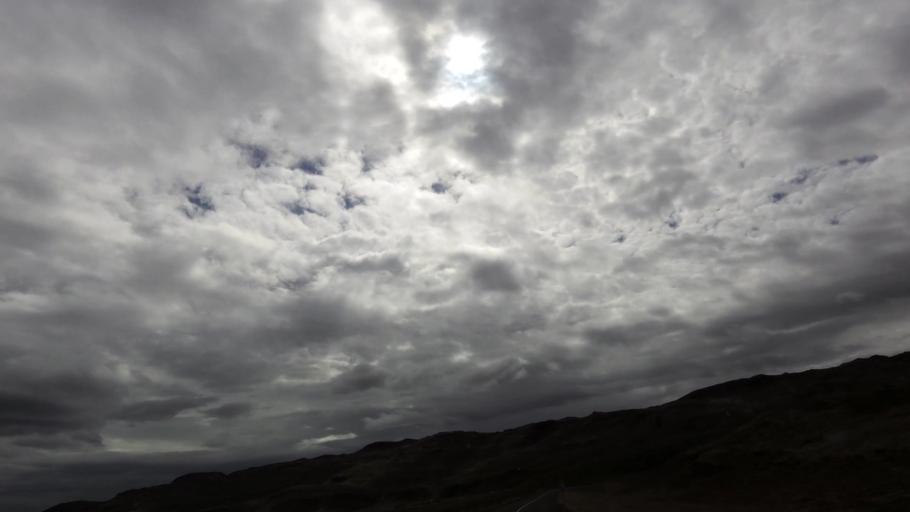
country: IS
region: West
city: Stykkisholmur
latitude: 65.5393
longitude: -22.1147
